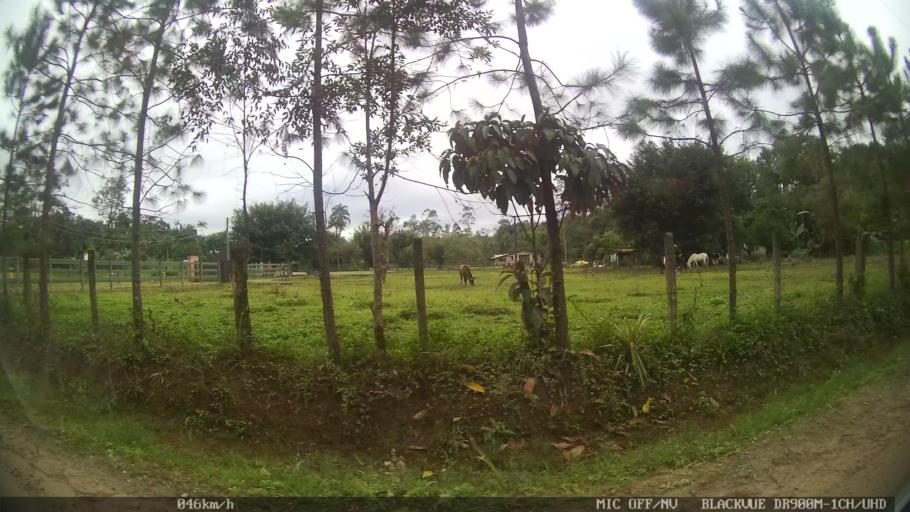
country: BR
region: Santa Catarina
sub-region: Joinville
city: Joinville
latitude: -26.2683
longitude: -48.9320
